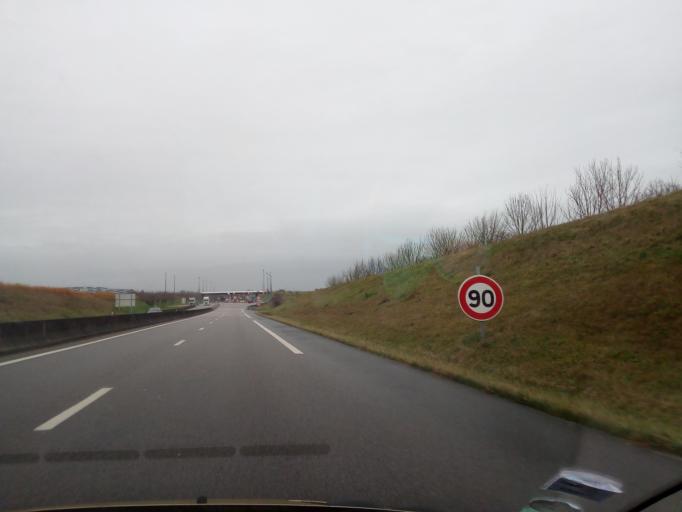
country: FR
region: Haute-Normandie
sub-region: Departement de l'Eure
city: Bourg-Achard
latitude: 49.3503
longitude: 0.8351
